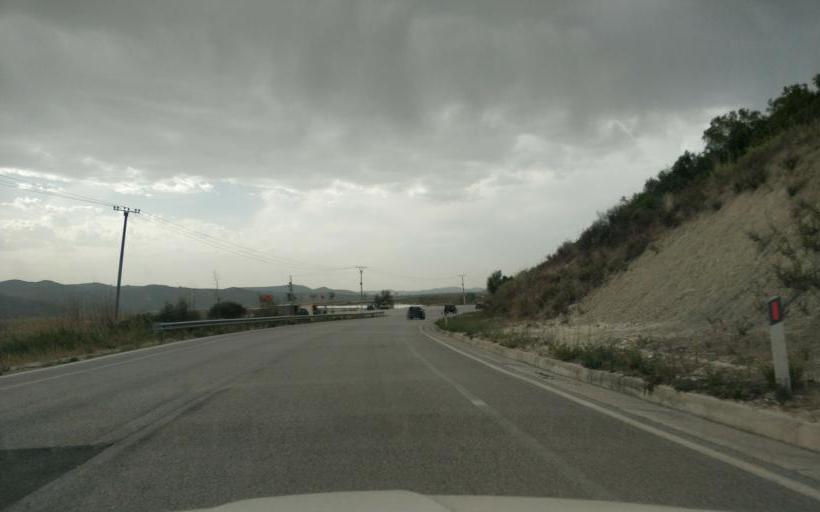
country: AL
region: Fier
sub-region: Rrethi i Mallakastres
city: Hekal
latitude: 40.5281
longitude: 19.7302
